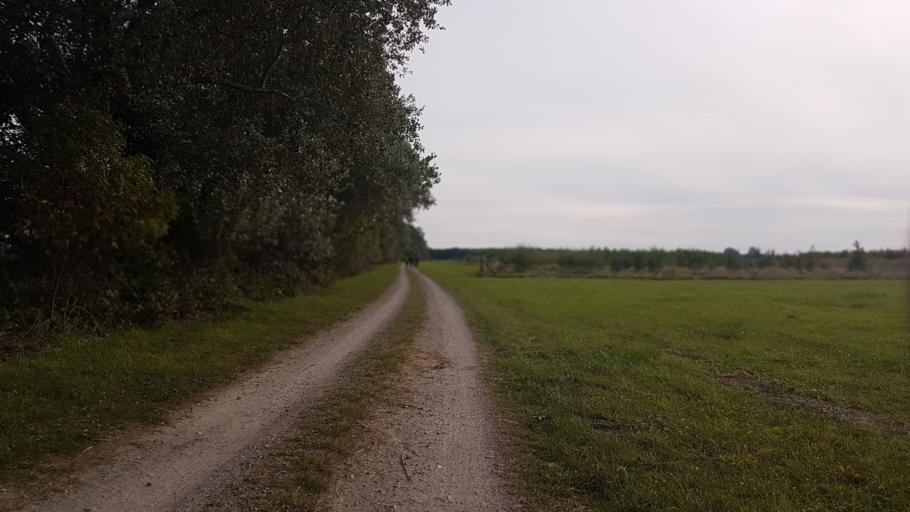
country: DE
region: Mecklenburg-Vorpommern
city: Hiddensee
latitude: 54.4872
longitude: 13.1620
